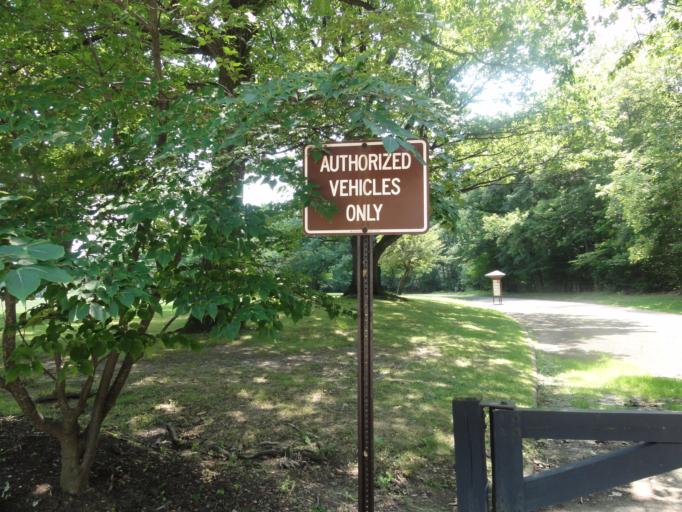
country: US
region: Ohio
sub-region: Cuyahoga County
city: Garfield Heights
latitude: 41.4311
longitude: -81.6024
